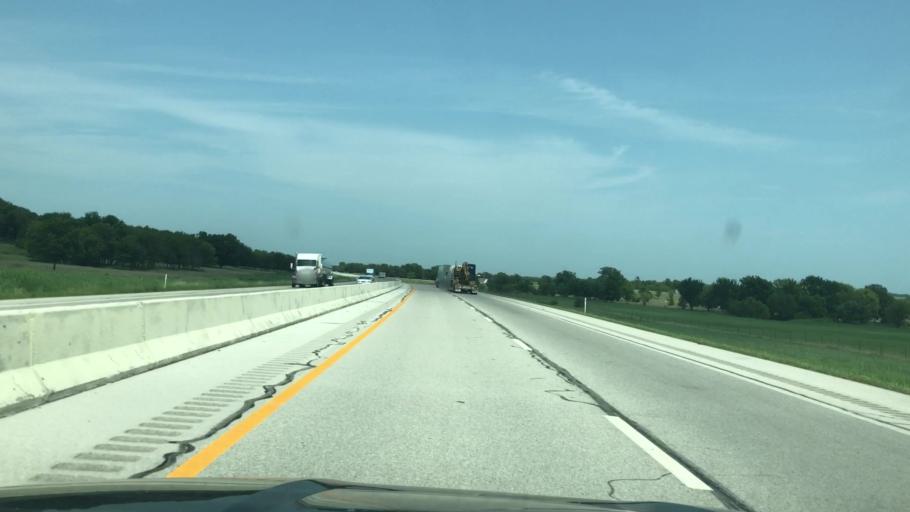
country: US
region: Oklahoma
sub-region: Rogers County
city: Bushyhead
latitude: 36.3525
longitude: -95.4614
